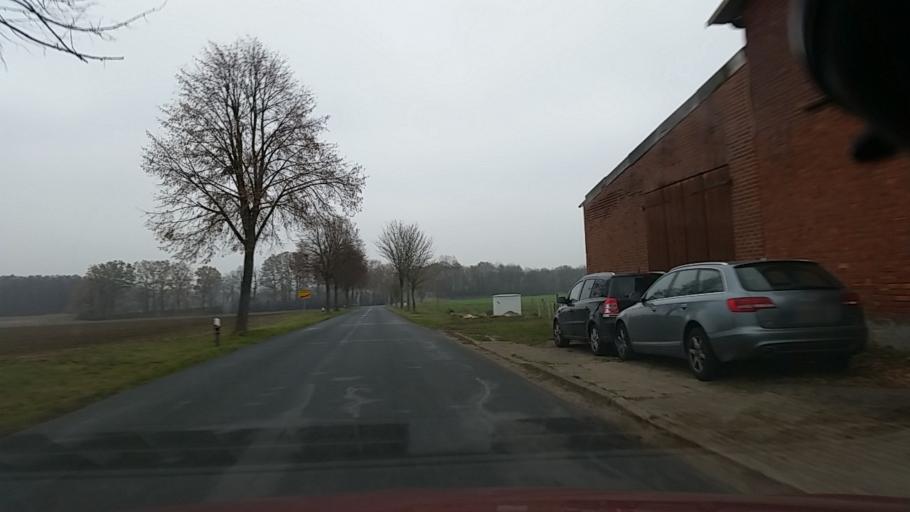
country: DE
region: Lower Saxony
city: Stadensen
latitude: 52.8519
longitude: 10.5663
